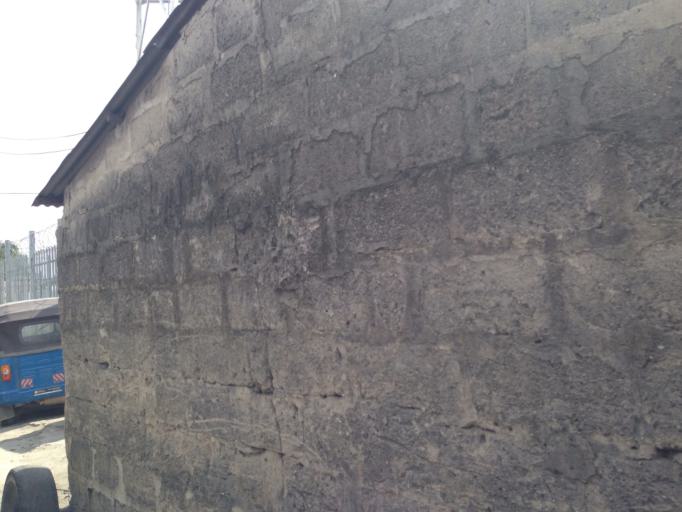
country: TZ
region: Dar es Salaam
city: Dar es Salaam
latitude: -6.8422
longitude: 39.2809
